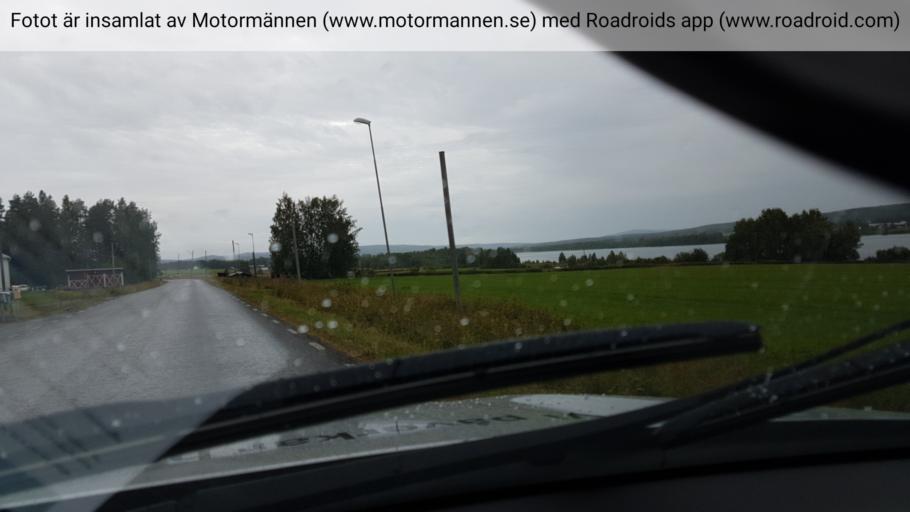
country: SE
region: Norrbotten
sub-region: Bodens Kommun
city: Boden
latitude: 65.8895
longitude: 21.3519
